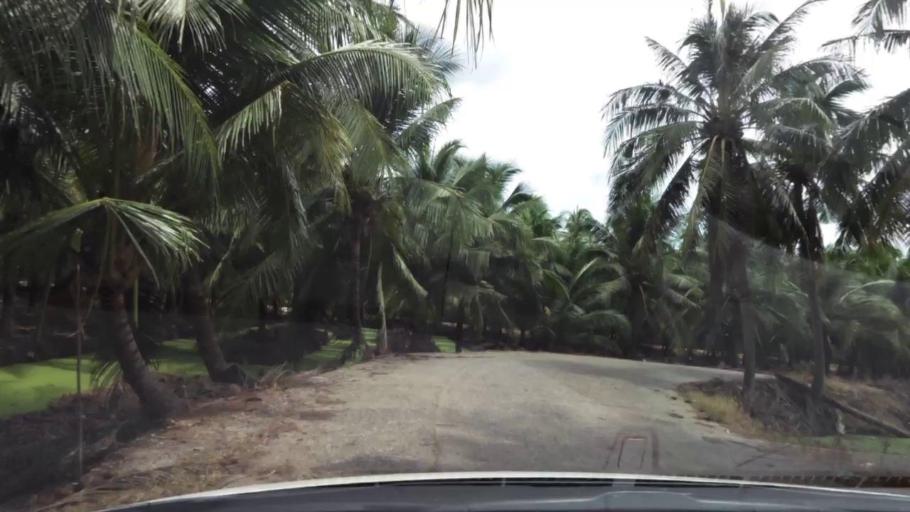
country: TH
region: Ratchaburi
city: Damnoen Saduak
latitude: 13.5224
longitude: 100.0047
